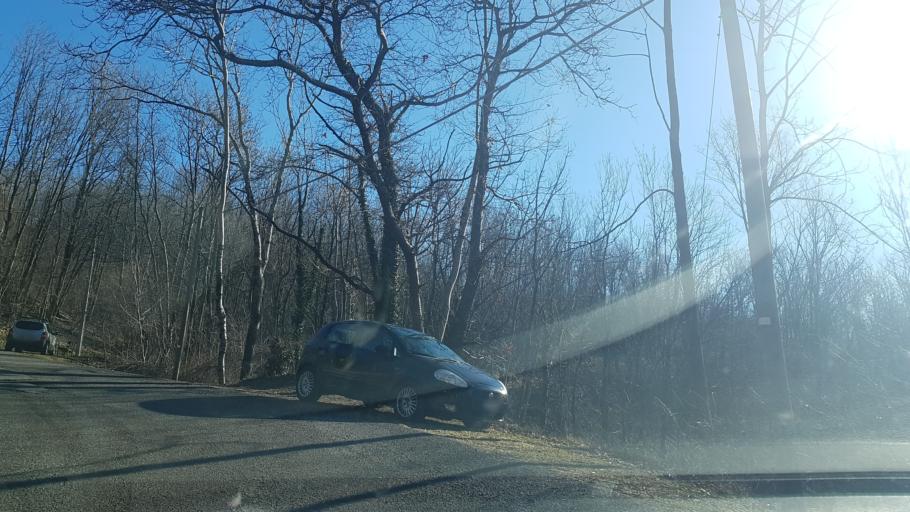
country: IT
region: Friuli Venezia Giulia
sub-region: Provincia di Udine
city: Isola
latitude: 46.2640
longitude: 13.1977
